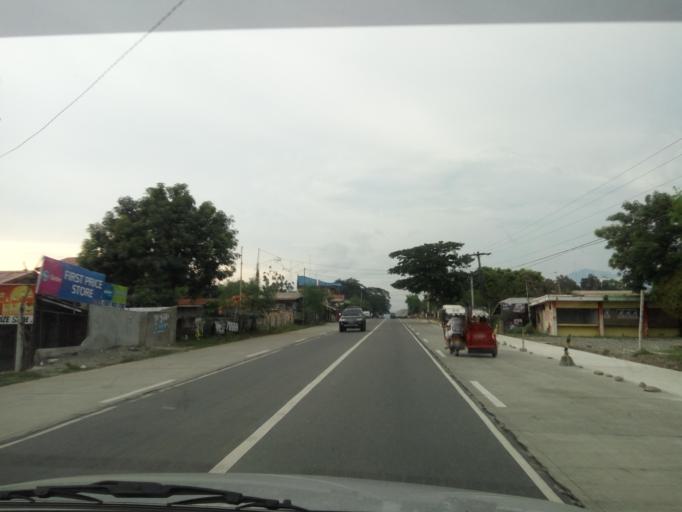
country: PH
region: Ilocos
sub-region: Province of Pangasinan
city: Bataquil
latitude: 16.1489
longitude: 120.5231
